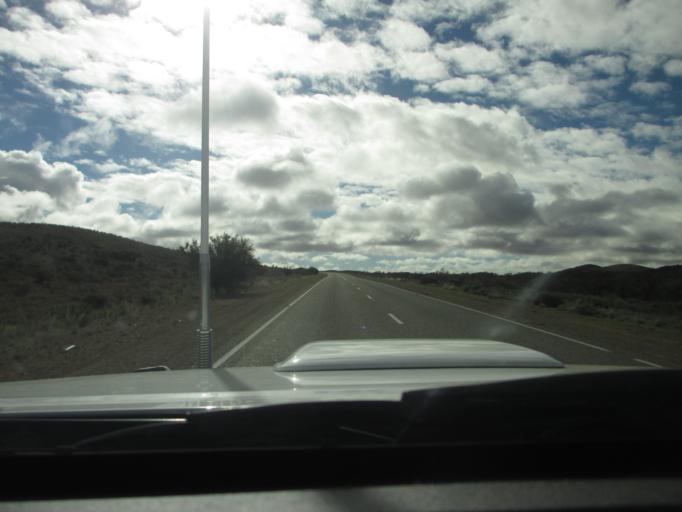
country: AU
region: South Australia
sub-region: Flinders Ranges
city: Quorn
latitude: -32.2061
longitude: 138.5266
